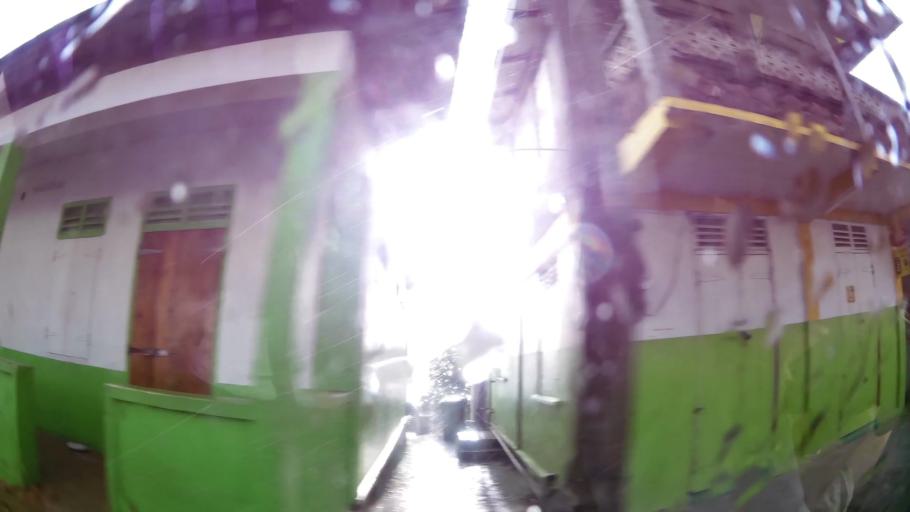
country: DM
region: Saint Paul
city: Mahaut
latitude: 15.3613
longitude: -61.3971
